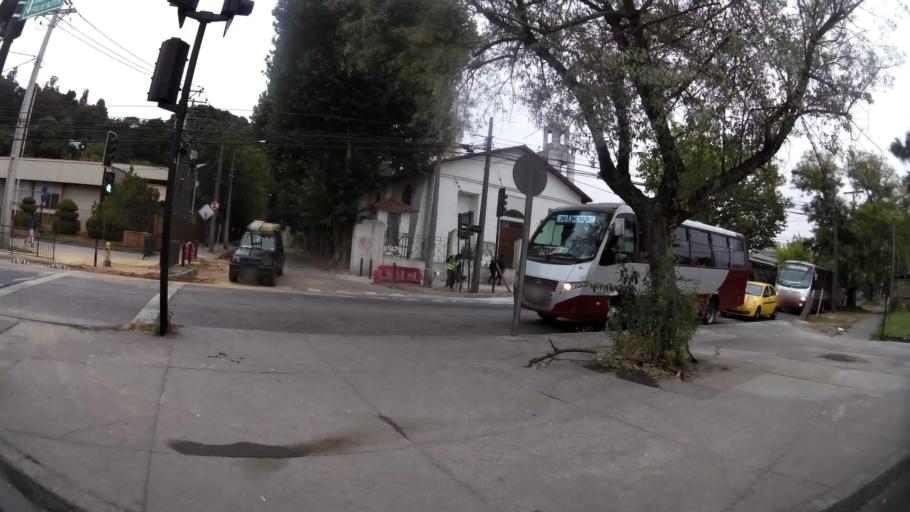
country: CL
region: Biobio
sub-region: Provincia de Concepcion
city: Concepcion
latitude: -36.8166
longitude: -73.0327
